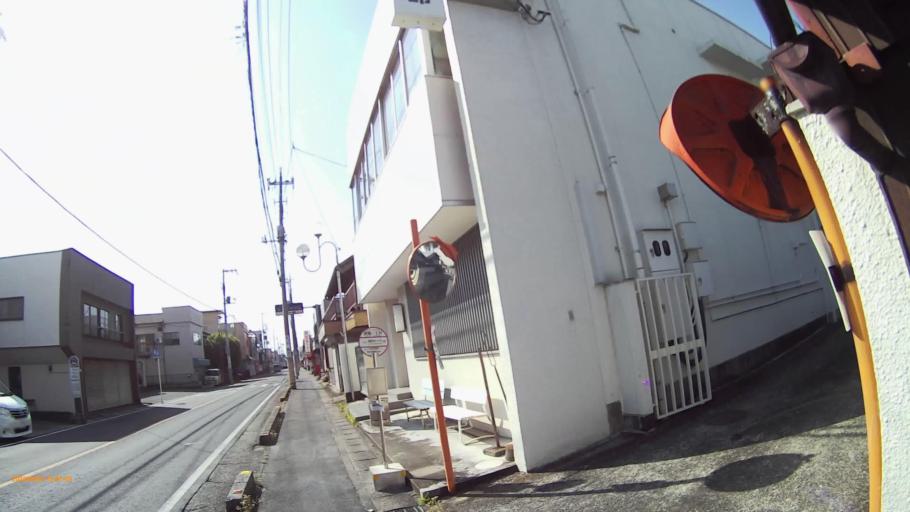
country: JP
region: Saitama
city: Sugito
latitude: 36.0272
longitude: 139.7322
